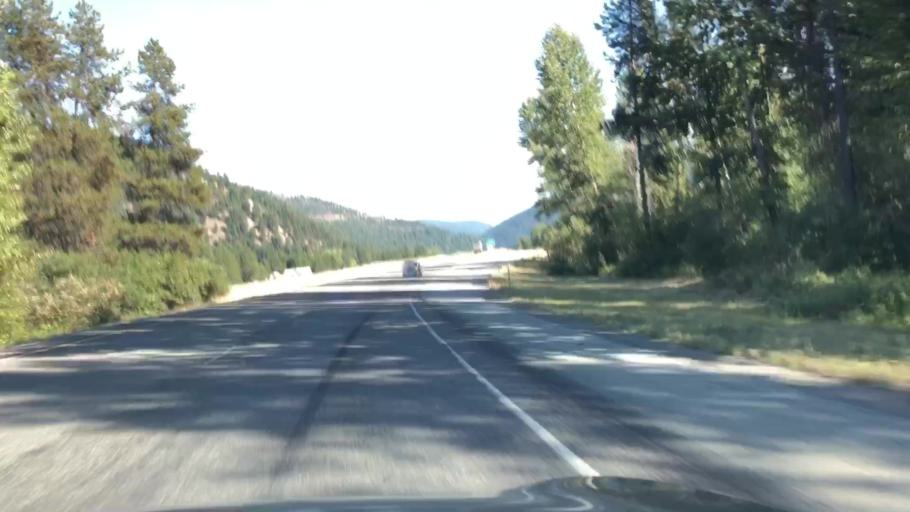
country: US
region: Montana
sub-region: Sanders County
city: Thompson Falls
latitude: 47.3779
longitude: -115.3547
